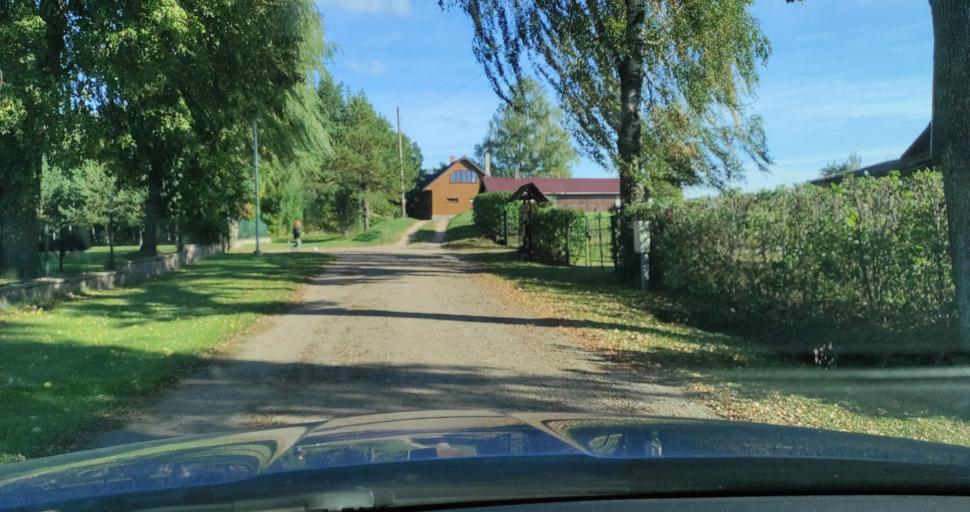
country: LV
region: Skrunda
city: Skrunda
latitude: 56.6814
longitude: 22.0198
